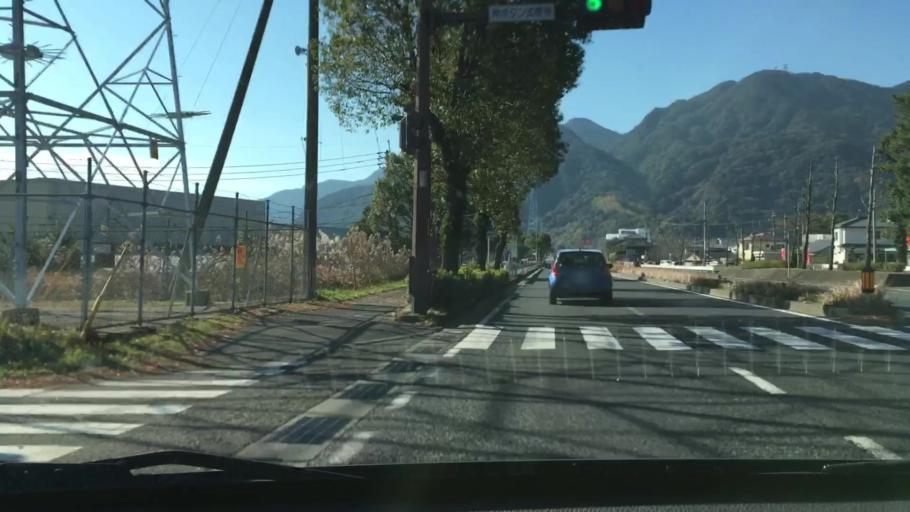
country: JP
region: Kagoshima
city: Kajiki
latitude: 31.7132
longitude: 130.6175
